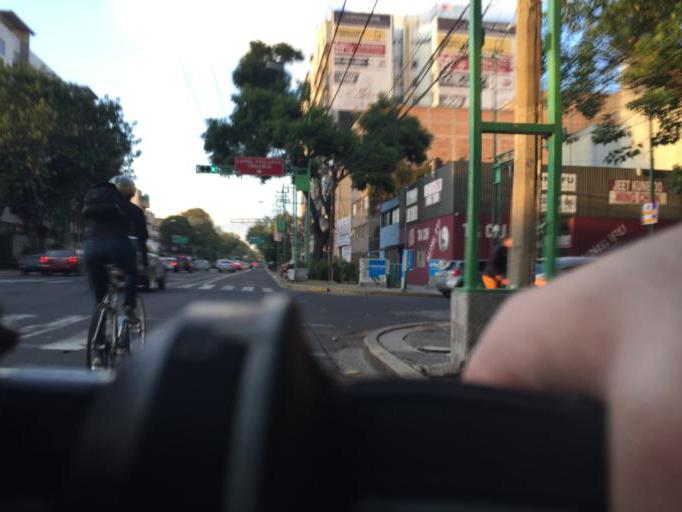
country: MX
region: Mexico City
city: Colonia Nativitas
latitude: 19.3743
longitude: -99.1492
